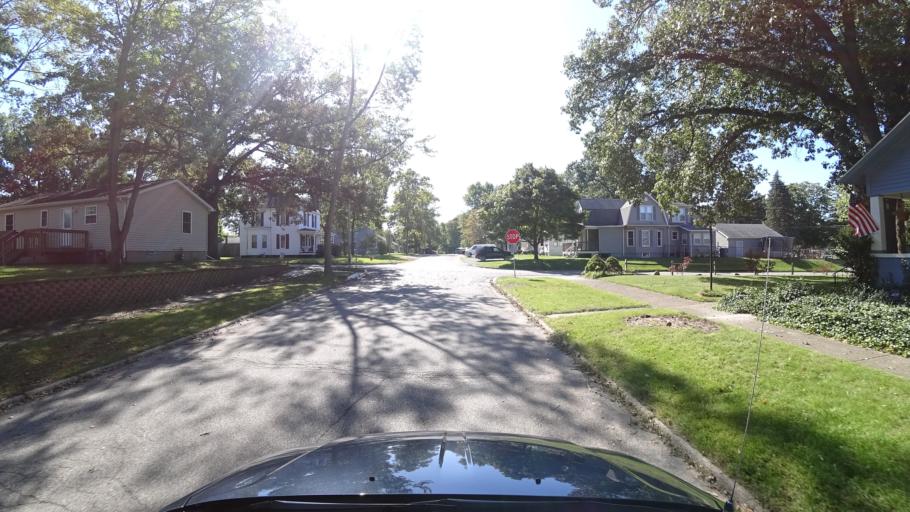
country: US
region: Indiana
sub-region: LaPorte County
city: Michigan City
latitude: 41.7062
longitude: -86.8807
